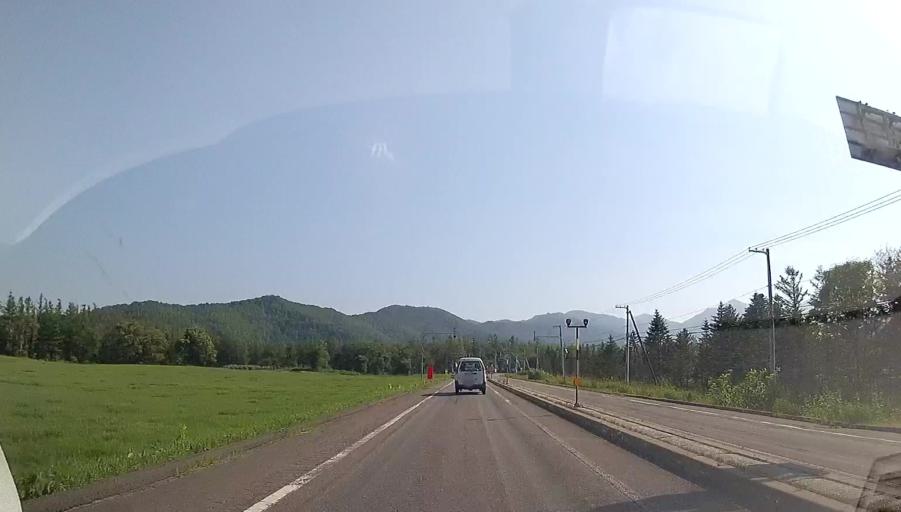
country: JP
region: Hokkaido
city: Otofuke
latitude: 42.9853
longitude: 142.8385
